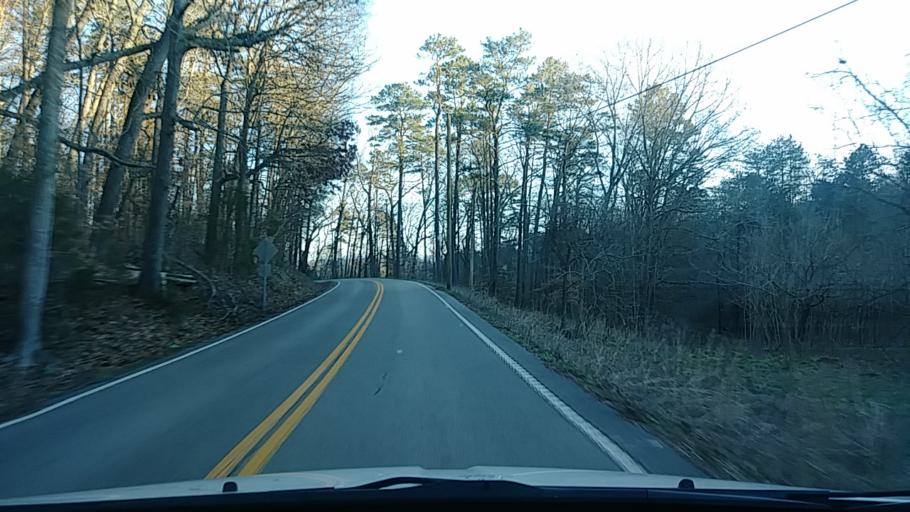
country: US
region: Tennessee
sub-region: Greene County
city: Mosheim
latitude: 36.1271
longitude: -83.1063
